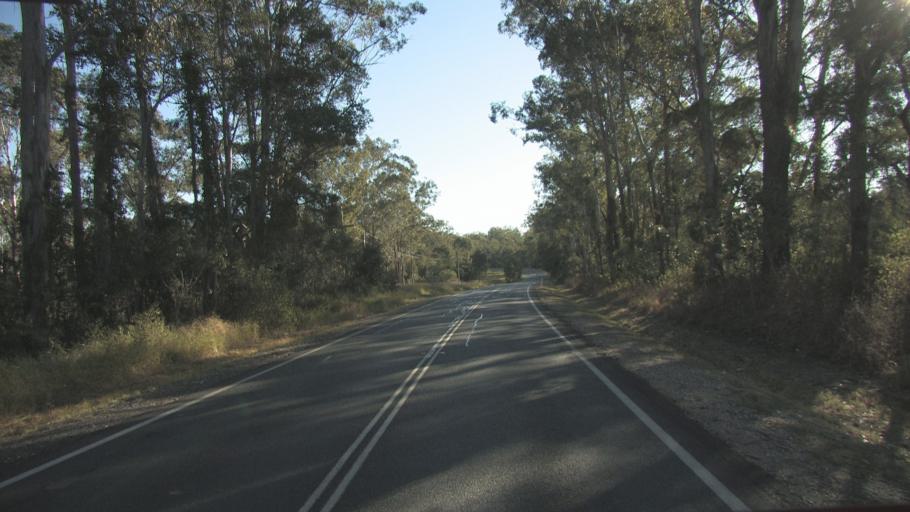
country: AU
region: Queensland
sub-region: Logan
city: Chambers Flat
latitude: -27.7808
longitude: 153.0638
